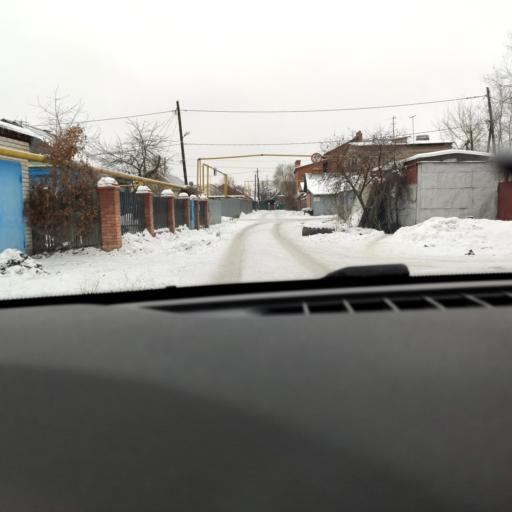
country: RU
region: Samara
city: Smyshlyayevka
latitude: 53.2320
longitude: 50.3031
